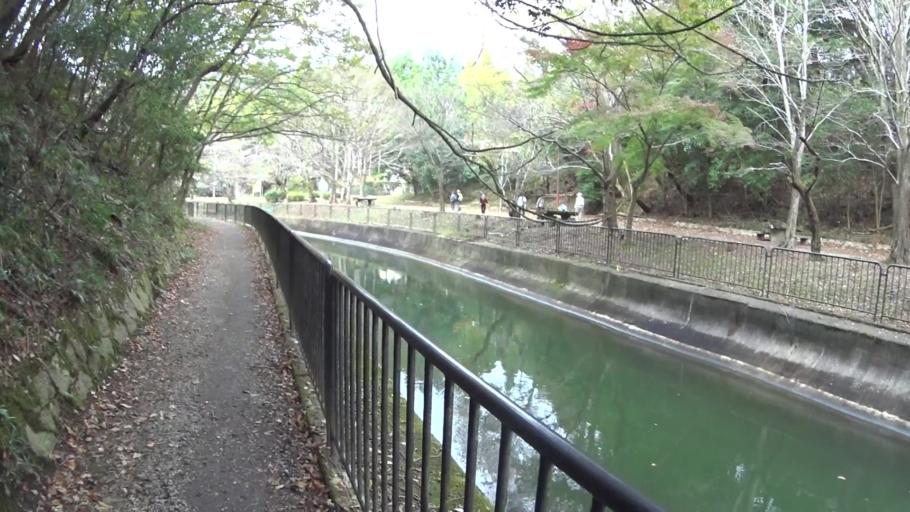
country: JP
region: Kyoto
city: Kyoto
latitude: 35.0001
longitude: 135.8034
